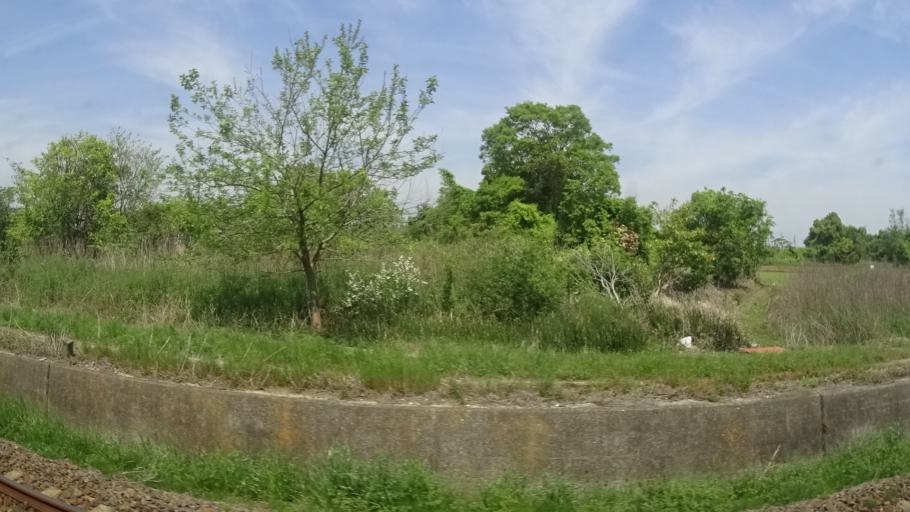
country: JP
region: Mie
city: Kawage
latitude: 34.8438
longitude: 136.5598
